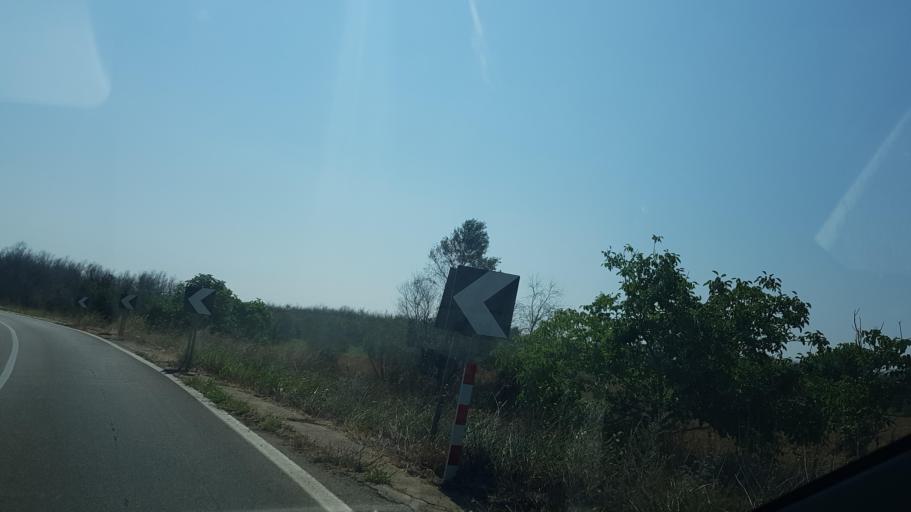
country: IT
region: Apulia
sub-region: Provincia di Lecce
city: Montesano Salentino
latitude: 40.0035
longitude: 18.3013
